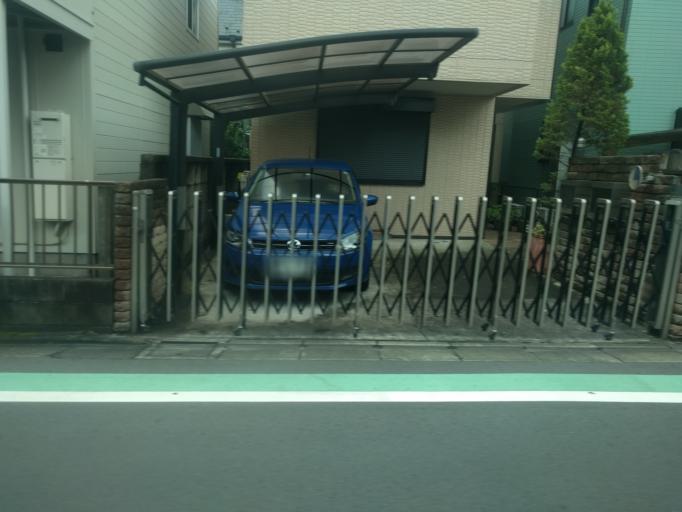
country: JP
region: Tokyo
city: Tokyo
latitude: 35.6054
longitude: 139.6759
